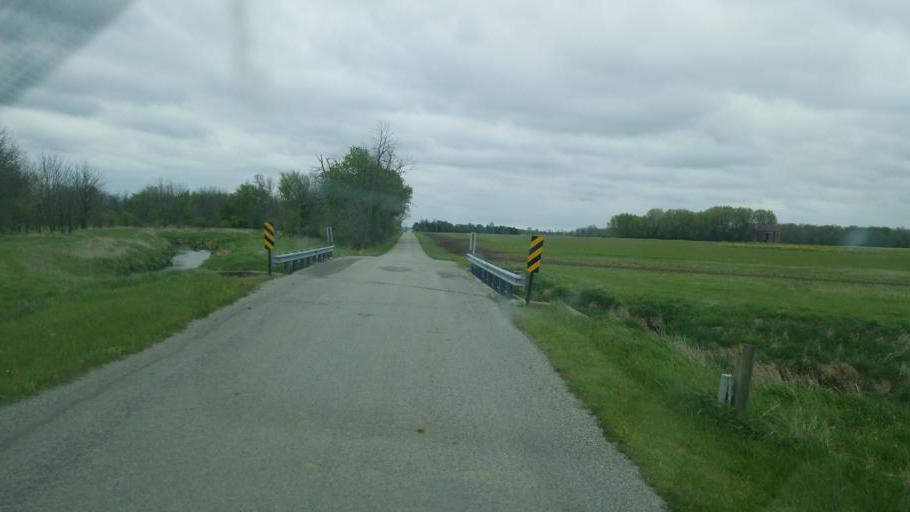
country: US
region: Ohio
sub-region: Hardin County
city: Kenton
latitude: 40.7294
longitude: -83.5951
